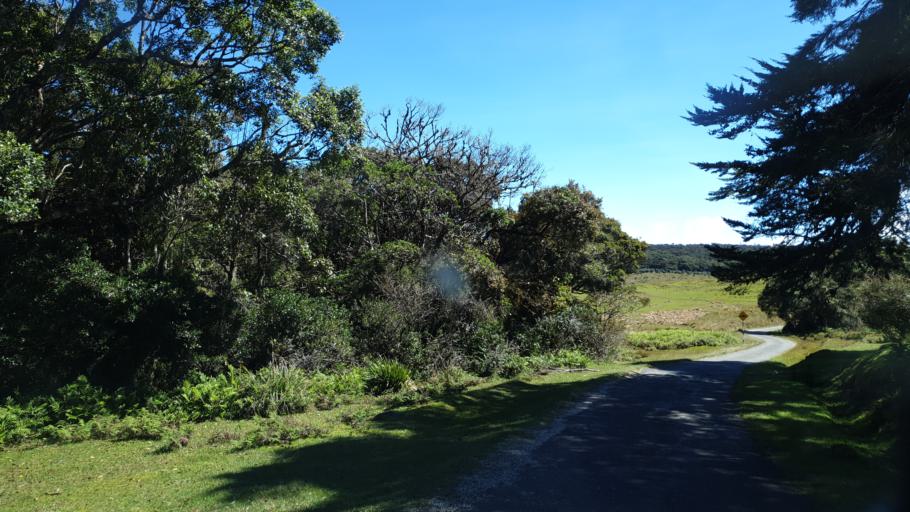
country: LK
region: Uva
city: Haputale
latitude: 6.7986
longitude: 80.8150
